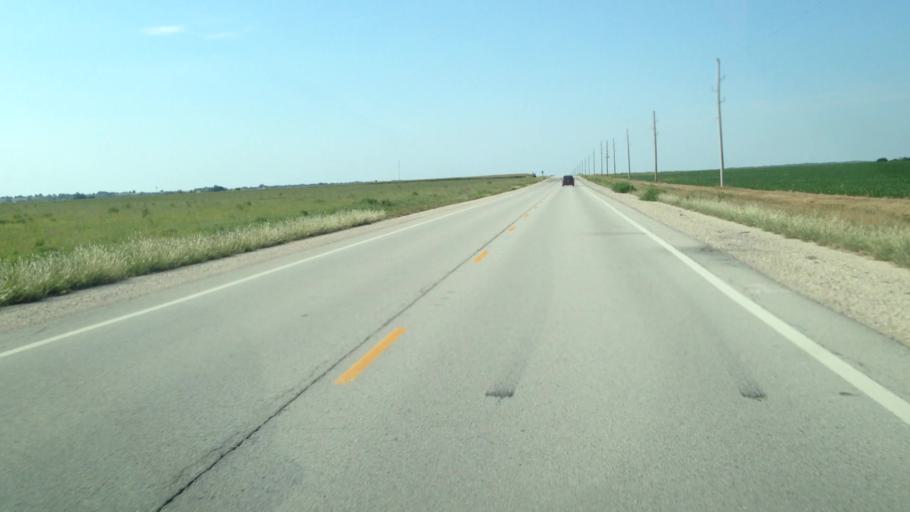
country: US
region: Kansas
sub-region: Anderson County
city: Garnett
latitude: 38.0481
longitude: -95.1695
